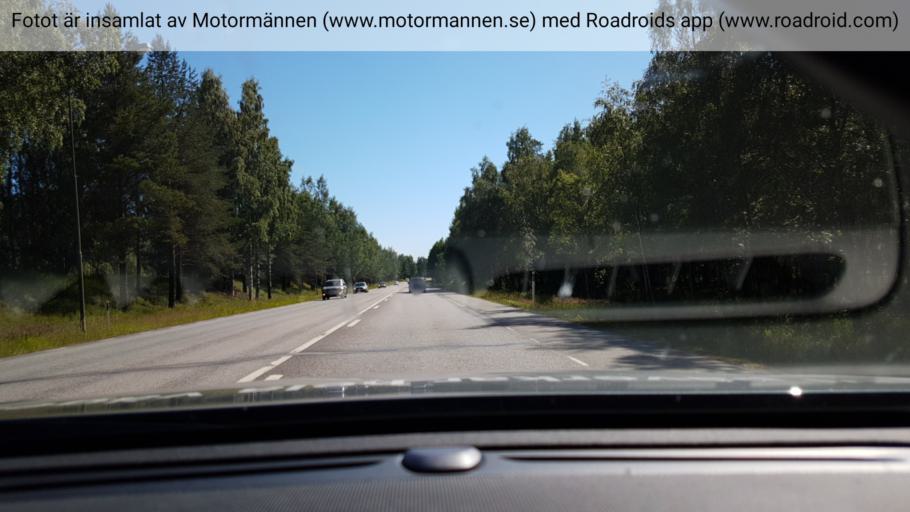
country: SE
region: Vaesterbotten
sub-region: Umea Kommun
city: Umea
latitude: 63.8428
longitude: 20.2771
